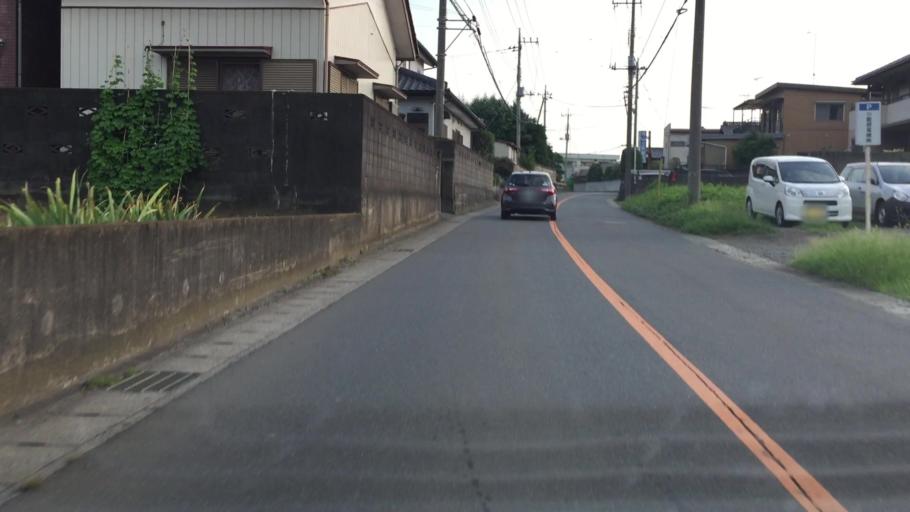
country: JP
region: Tochigi
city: Fujioka
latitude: 36.2727
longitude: 139.6539
